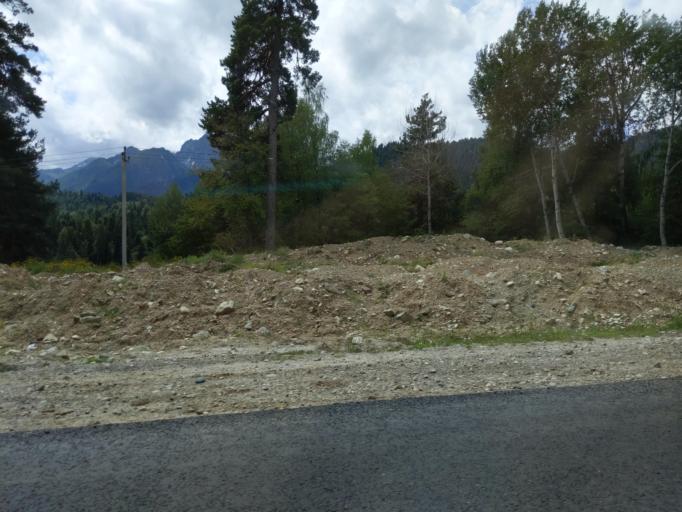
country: RU
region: Karachayevo-Cherkesiya
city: Nizhniy Arkhyz
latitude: 43.5371
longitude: 41.2150
